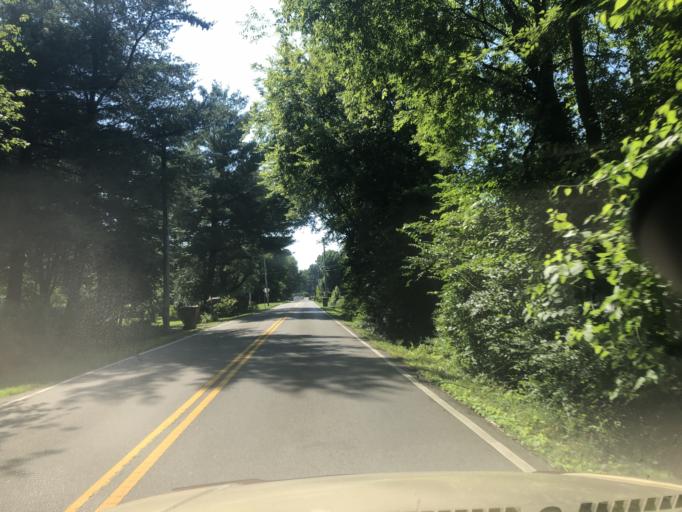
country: US
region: Tennessee
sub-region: Davidson County
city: Lakewood
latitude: 36.2361
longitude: -86.7035
